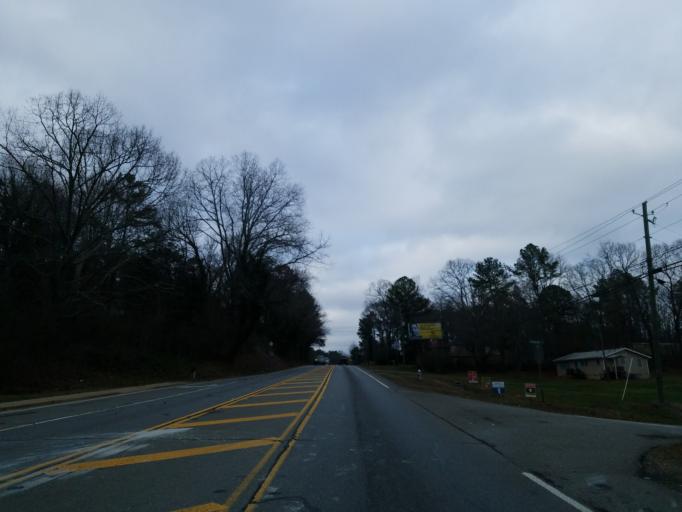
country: US
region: Georgia
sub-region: Cherokee County
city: Canton
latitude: 34.2583
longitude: -84.4940
